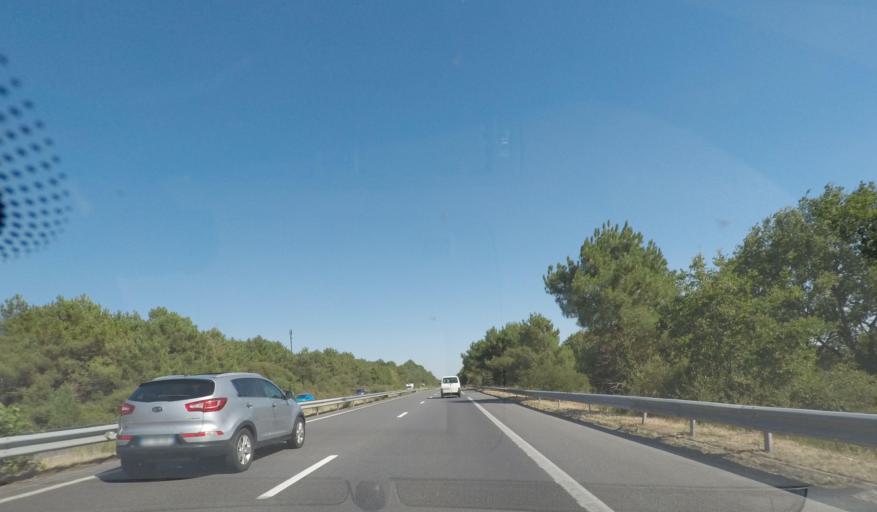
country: FR
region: Pays de la Loire
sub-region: Departement de la Loire-Atlantique
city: La Chapelle-des-Marais
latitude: 47.4949
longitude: -2.2466
